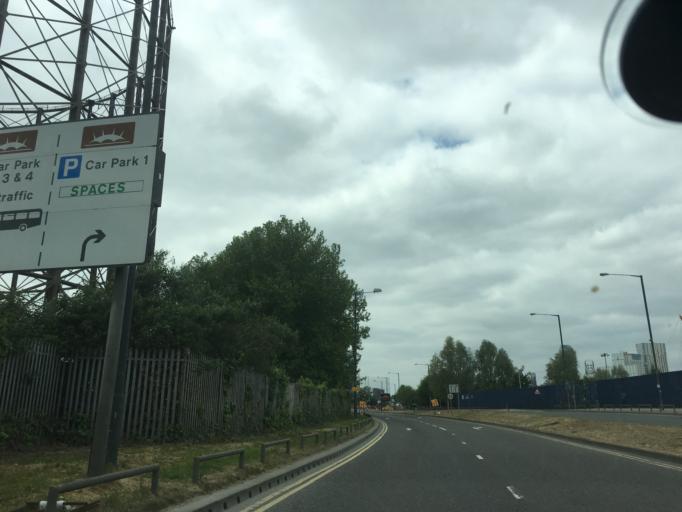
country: GB
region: England
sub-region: Greater London
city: Poplar
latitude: 51.4963
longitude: 0.0063
